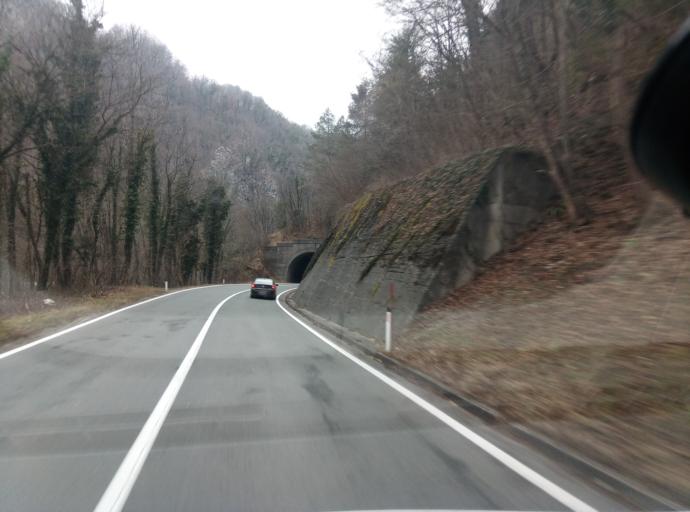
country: SI
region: Zagorje ob Savi
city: Kisovec
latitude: 46.1021
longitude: 14.9613
